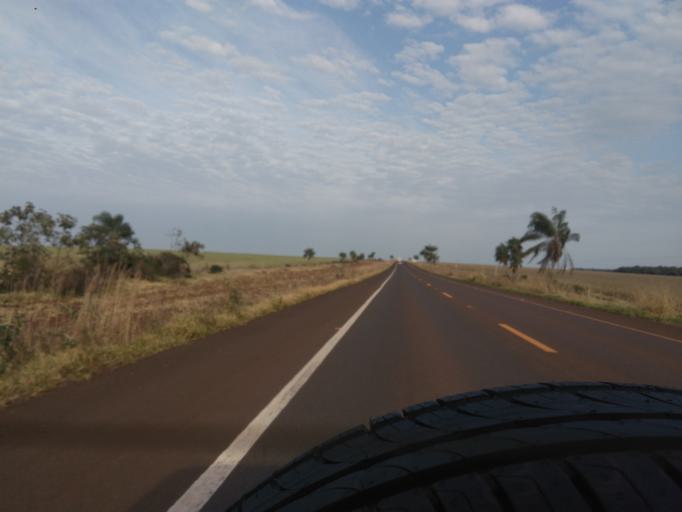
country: BR
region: Mato Grosso do Sul
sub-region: Ponta Pora
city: Ponta Pora
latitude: -22.5934
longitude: -55.5281
